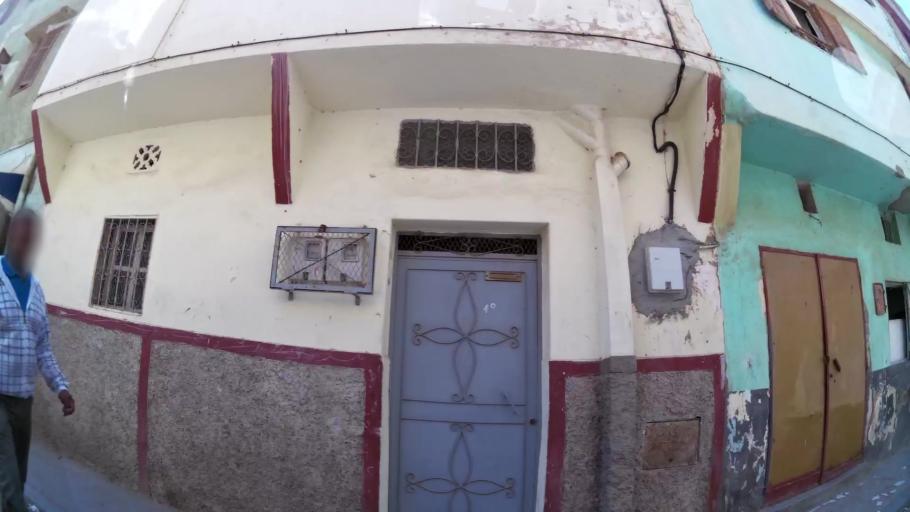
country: MA
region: Rabat-Sale-Zemmour-Zaer
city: Sale
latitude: 34.0367
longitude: -6.7988
